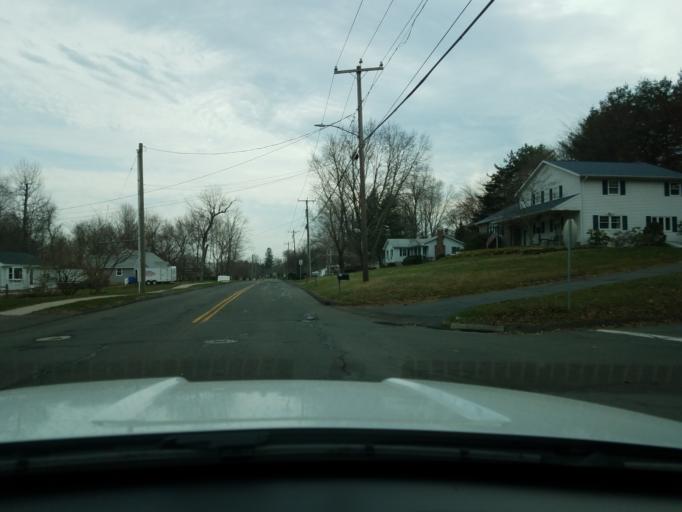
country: US
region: Connecticut
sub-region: Middlesex County
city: Cromwell
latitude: 41.6217
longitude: -72.6683
